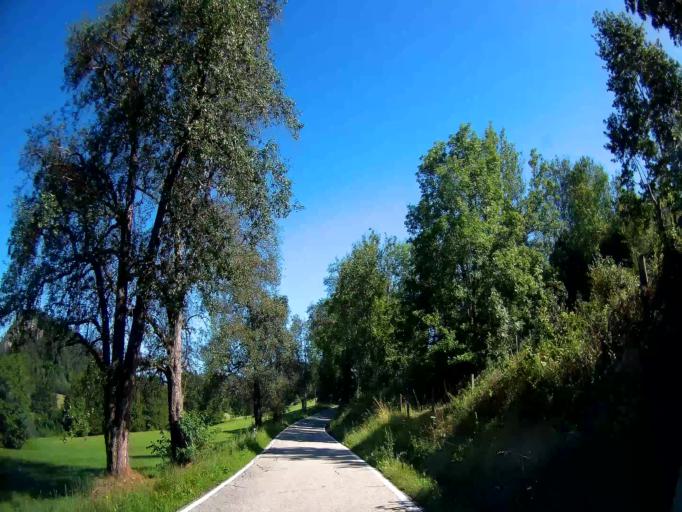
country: AT
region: Carinthia
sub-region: Politischer Bezirk Volkermarkt
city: Voelkermarkt
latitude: 46.6894
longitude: 14.5777
